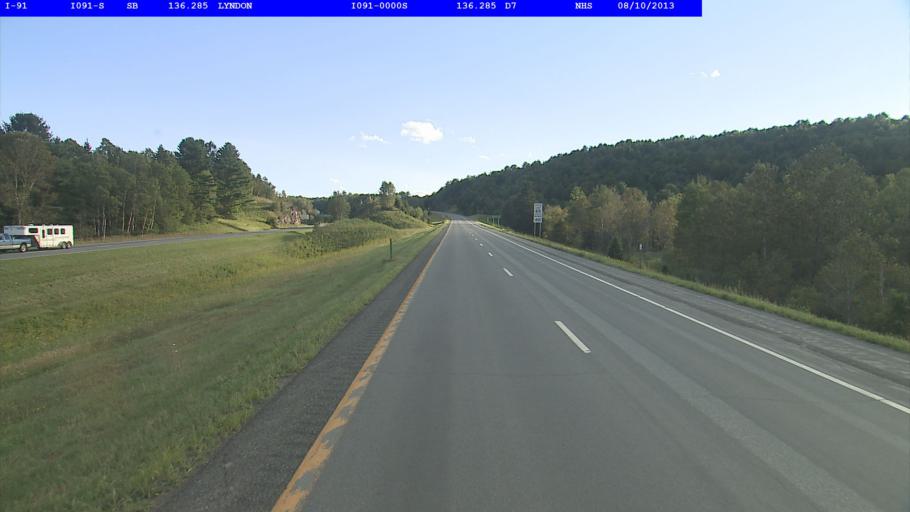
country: US
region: Vermont
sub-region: Caledonia County
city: Lyndon
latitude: 44.5065
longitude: -72.0149
